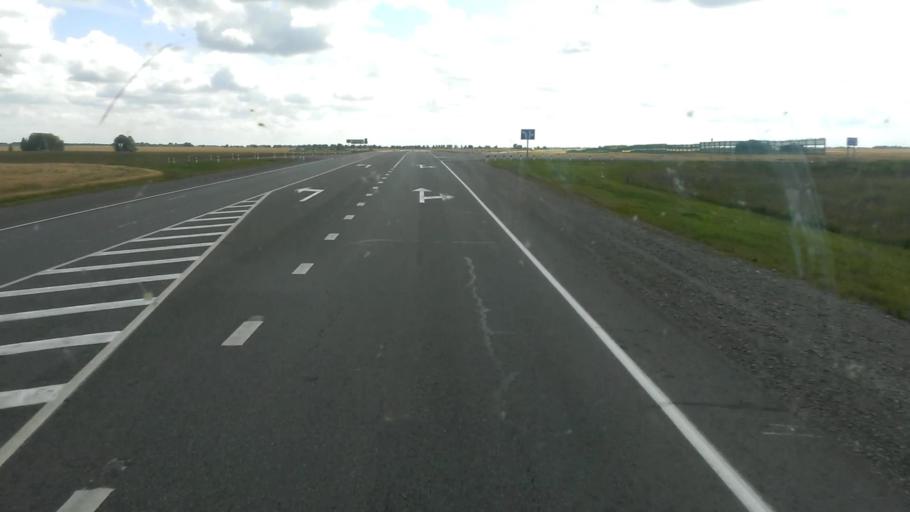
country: RU
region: Altai Krai
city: Troitskoye
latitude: 52.9173
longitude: 84.8115
